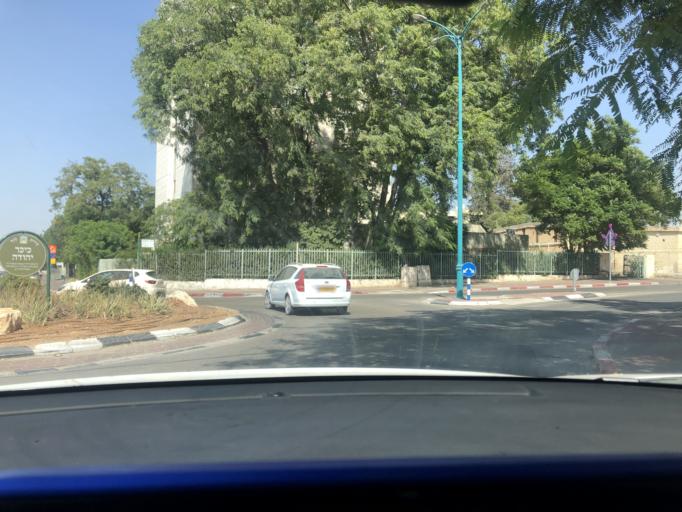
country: IL
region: Central District
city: Lod
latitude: 31.9482
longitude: 34.8815
